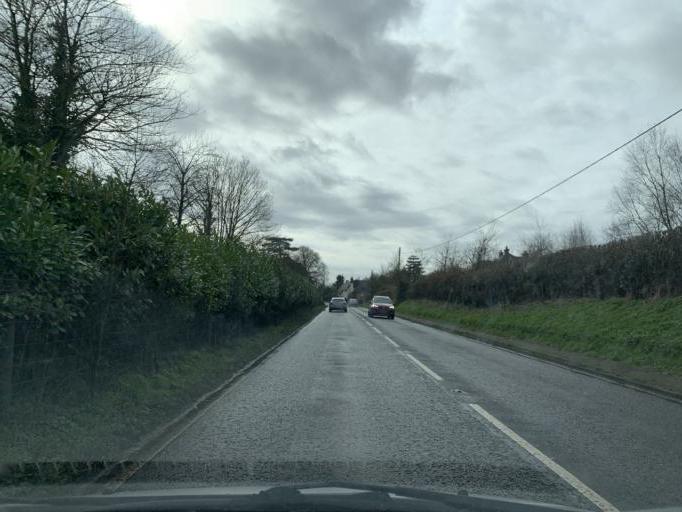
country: GB
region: England
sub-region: Hampshire
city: Fordingbridge
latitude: 50.9426
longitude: -1.7834
